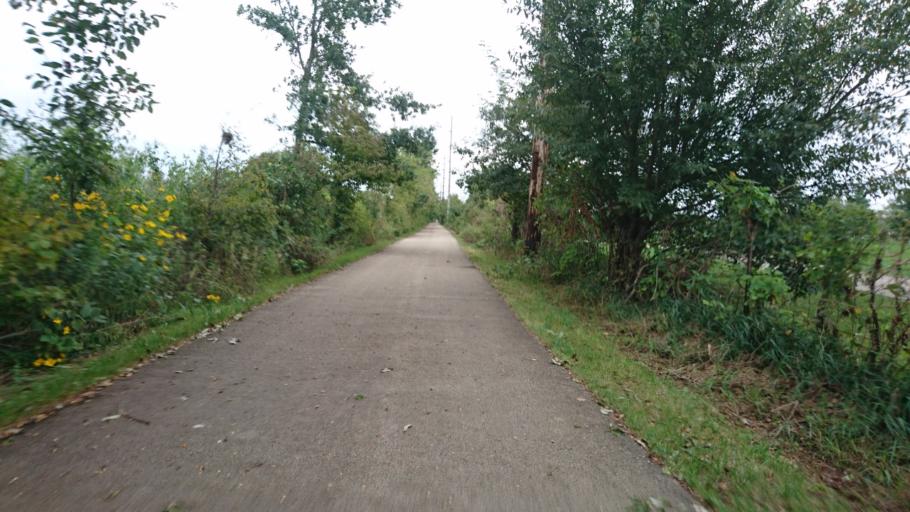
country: US
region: Illinois
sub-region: Sangamon County
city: Chatham
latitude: 39.6929
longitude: -89.6947
